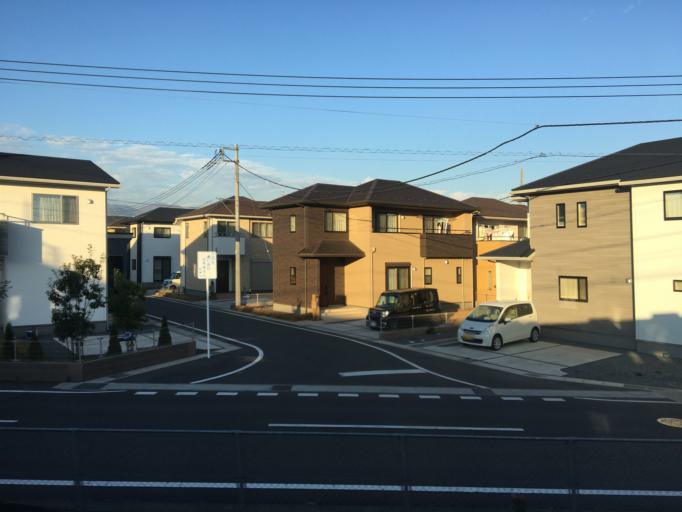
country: JP
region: Gunma
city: Maebashi-shi
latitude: 36.3755
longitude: 139.1012
